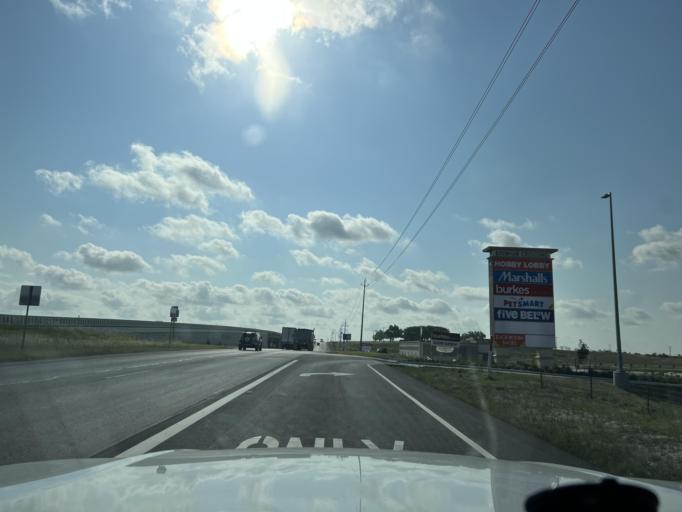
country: US
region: Texas
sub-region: Washington County
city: Brenham
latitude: 30.1410
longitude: -96.3850
